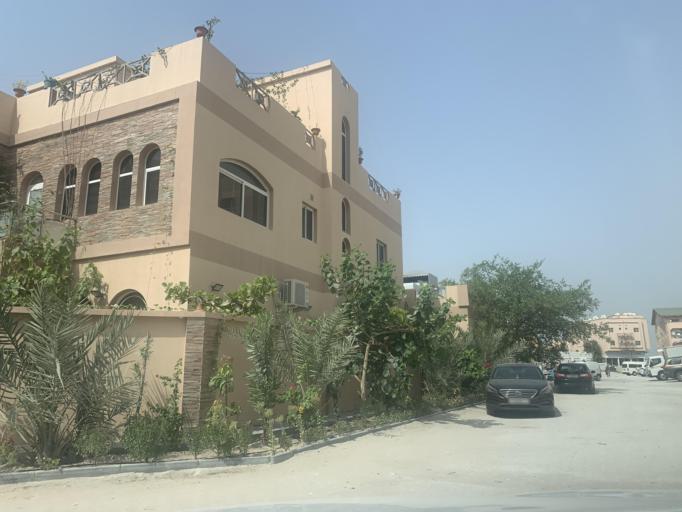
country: BH
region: Manama
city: Jidd Hafs
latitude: 26.2169
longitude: 50.4715
